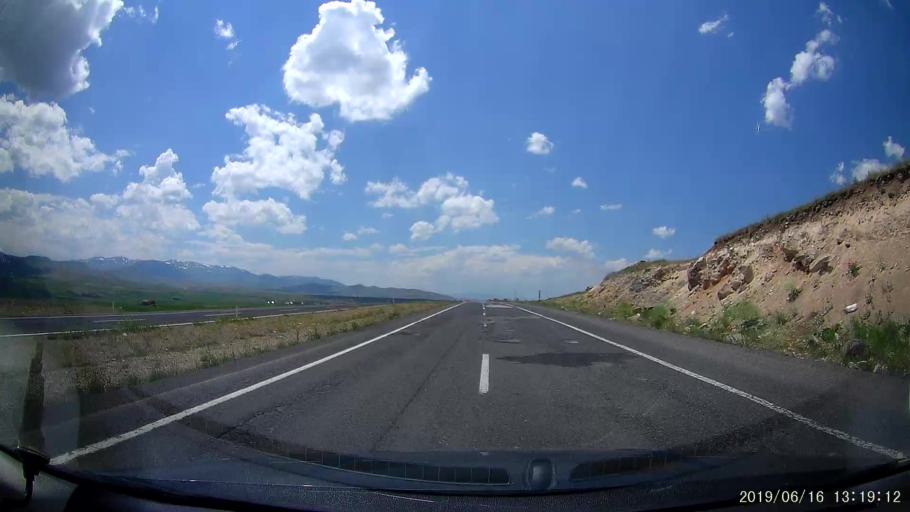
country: TR
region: Agri
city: Taslicay
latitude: 39.6328
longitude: 43.4132
